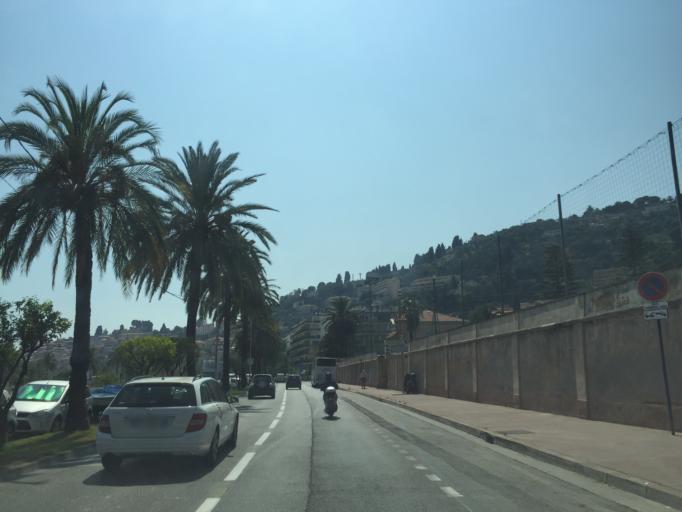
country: FR
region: Provence-Alpes-Cote d'Azur
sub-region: Departement des Alpes-Maritimes
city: Menton
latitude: 43.7834
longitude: 7.5142
